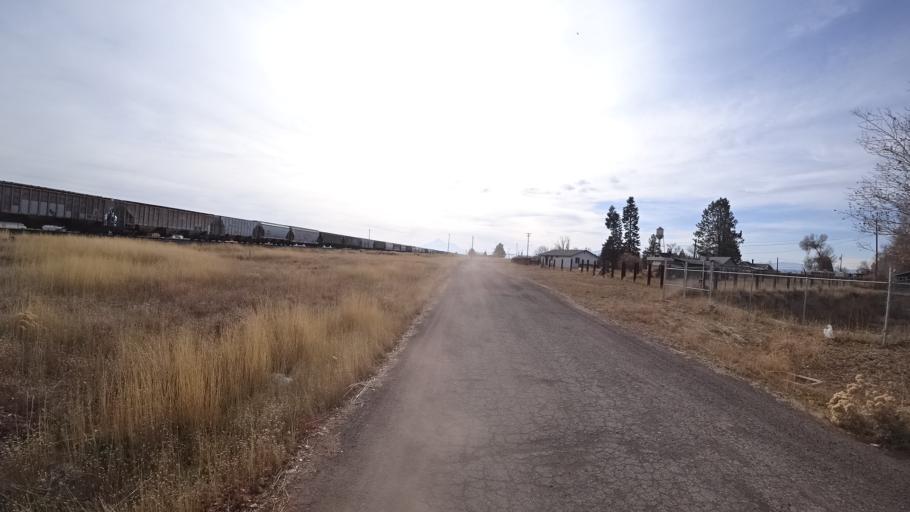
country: US
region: Oregon
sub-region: Klamath County
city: Klamath Falls
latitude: 41.9621
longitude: -121.9187
